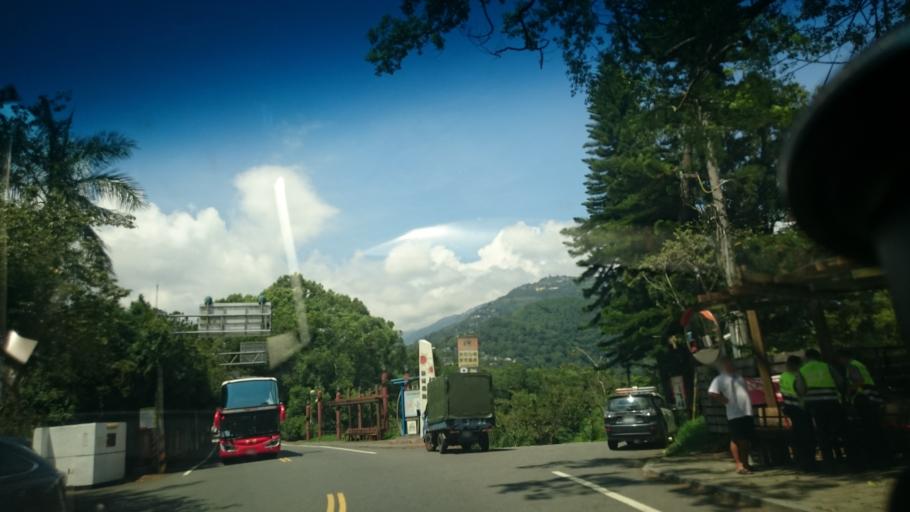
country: TW
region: Taiwan
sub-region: Nantou
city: Puli
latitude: 24.0179
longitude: 121.1307
